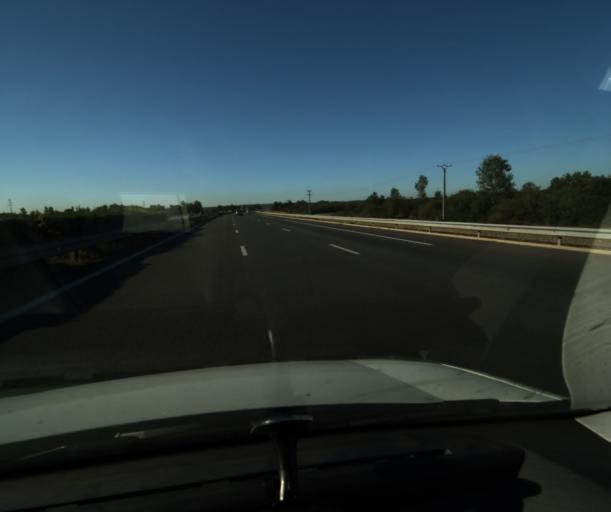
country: FR
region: Midi-Pyrenees
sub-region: Departement du Tarn-et-Garonne
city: Campsas
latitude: 43.8695
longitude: 1.3182
